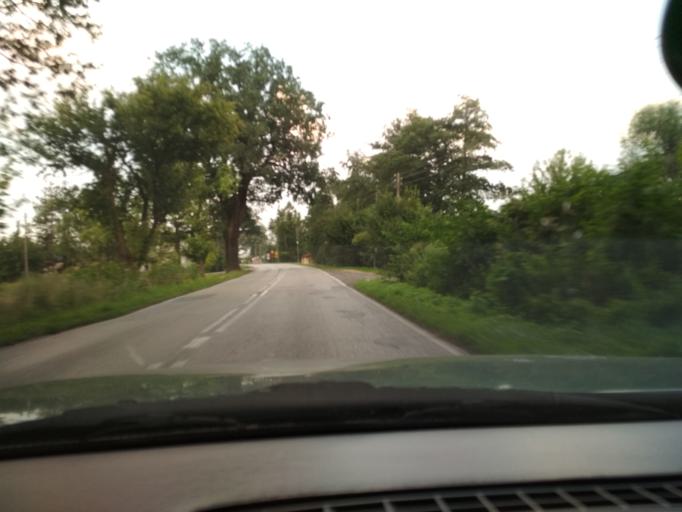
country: PL
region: Silesian Voivodeship
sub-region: Powiat cieszynski
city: Zablocie
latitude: 49.8981
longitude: 18.7949
